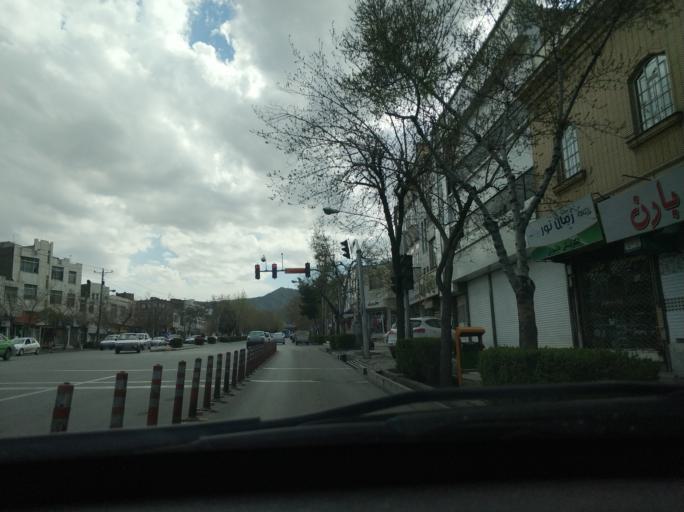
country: IR
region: Razavi Khorasan
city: Mashhad
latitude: 36.2676
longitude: 59.5872
